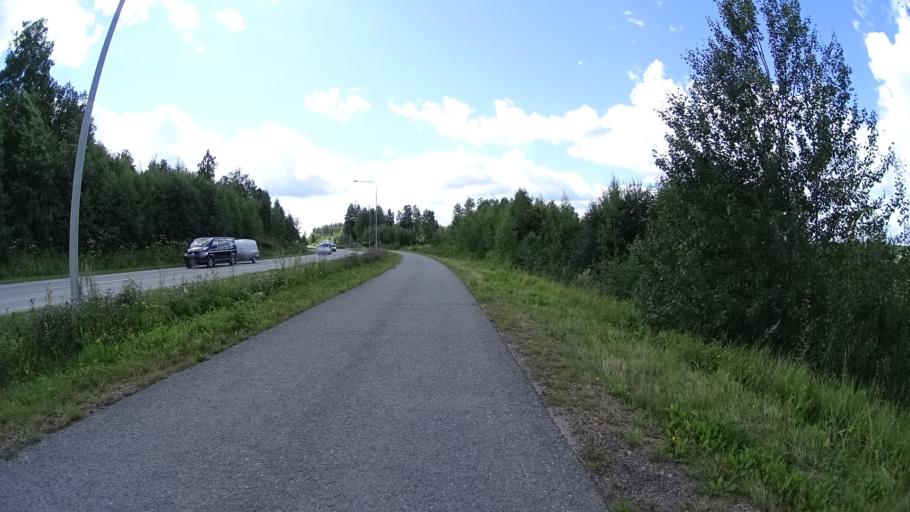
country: FI
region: Uusimaa
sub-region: Helsinki
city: Teekkarikylae
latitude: 60.3064
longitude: 24.8837
